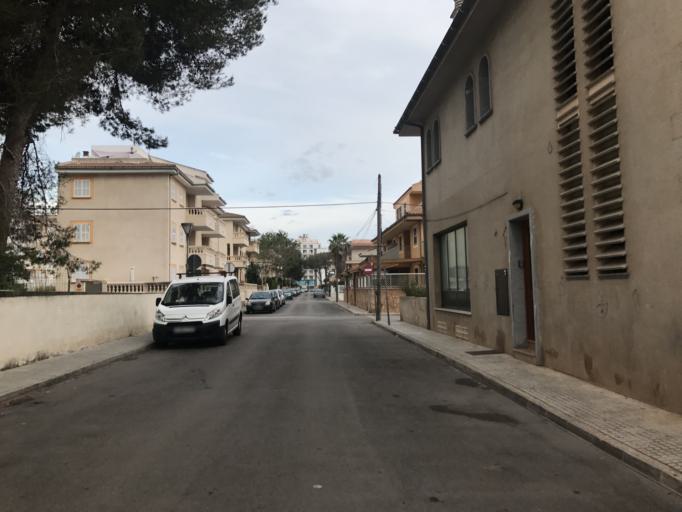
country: ES
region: Balearic Islands
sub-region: Illes Balears
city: Santa Margalida
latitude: 39.7626
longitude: 3.1537
